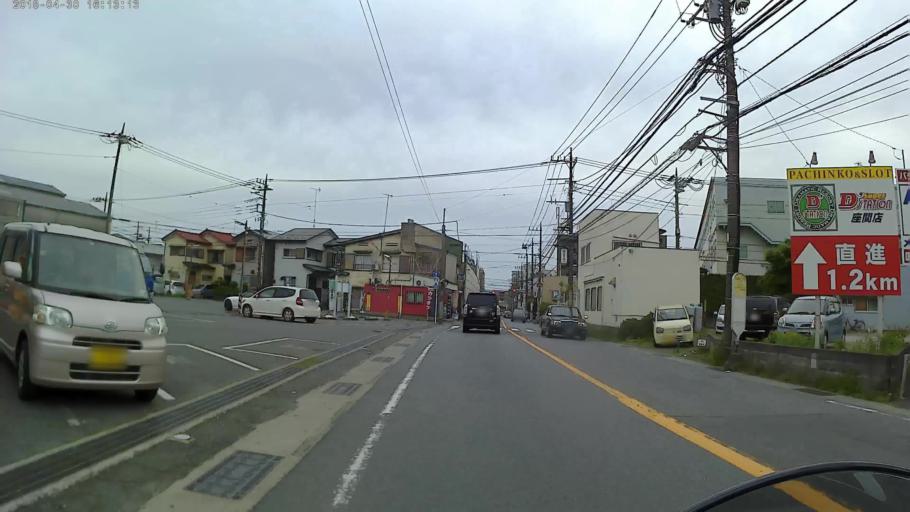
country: JP
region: Kanagawa
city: Minami-rinkan
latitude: 35.4910
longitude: 139.4314
